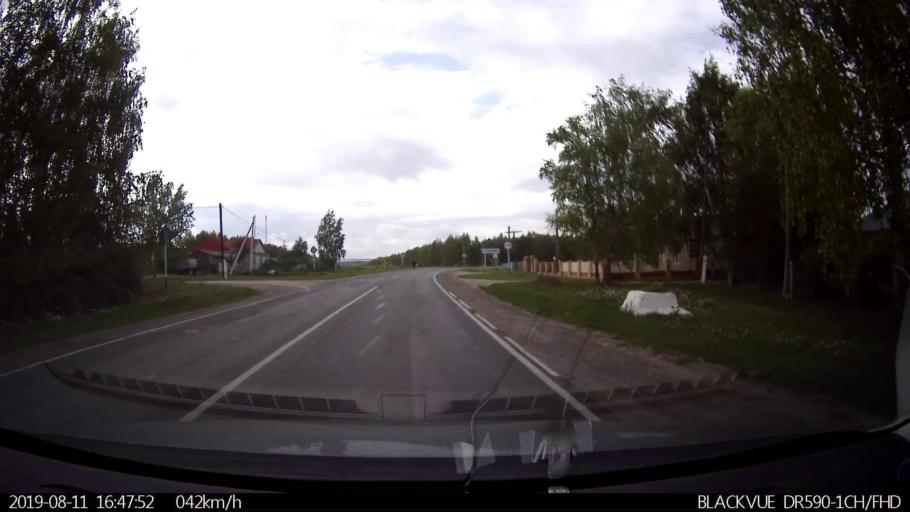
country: RU
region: Ulyanovsk
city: Mayna
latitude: 54.2052
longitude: 47.6926
